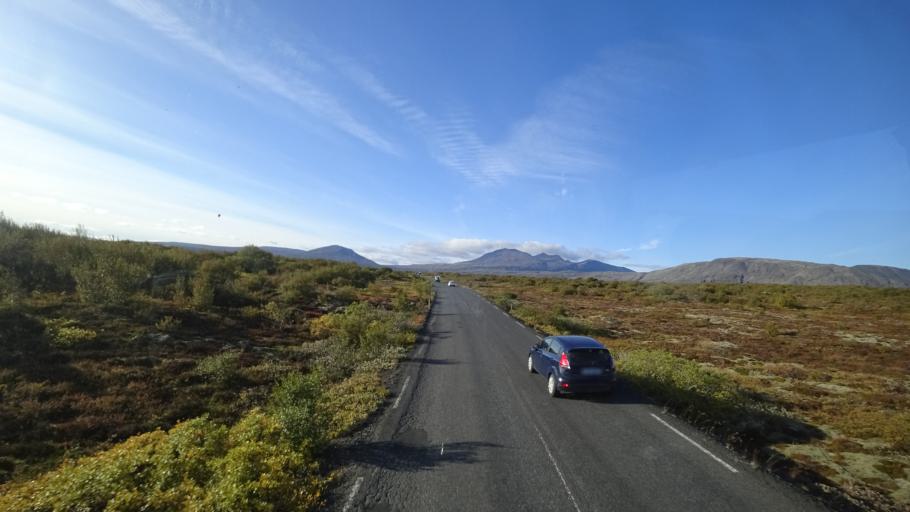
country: IS
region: South
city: Hveragerdi
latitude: 64.2643
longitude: -21.0554
